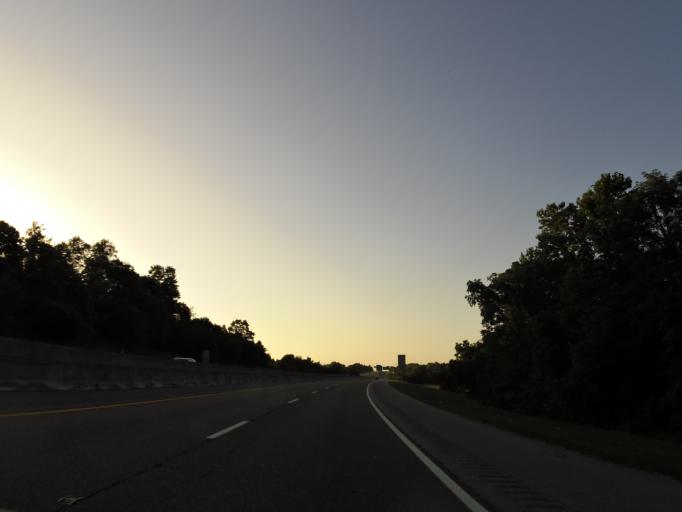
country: US
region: Tennessee
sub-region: Knox County
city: Farragut
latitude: 35.8937
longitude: -84.1151
